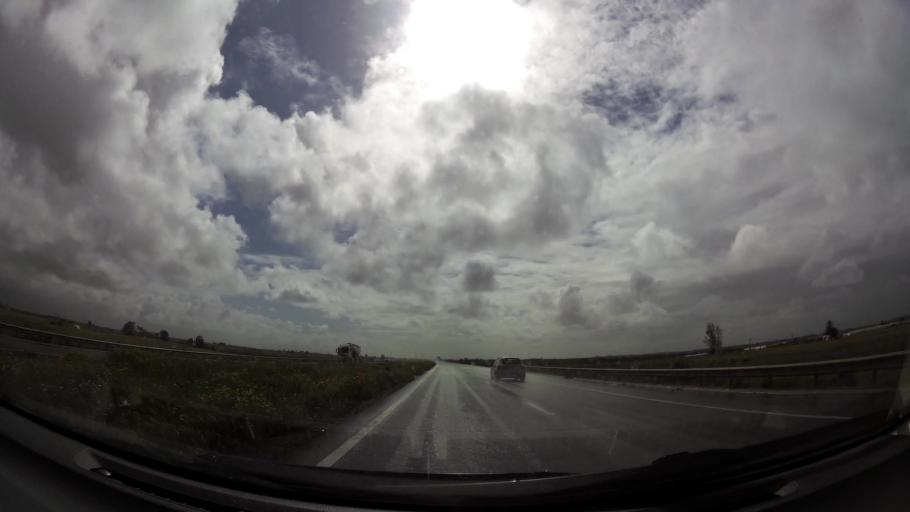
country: MA
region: Grand Casablanca
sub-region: Nouaceur
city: Dar Bouazza
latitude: 33.3647
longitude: -7.9328
